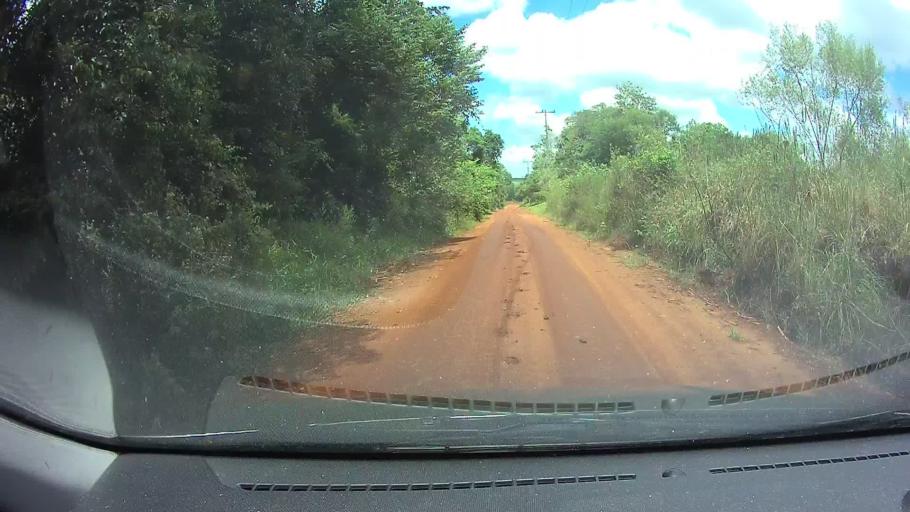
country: PY
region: Paraguari
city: La Colmena
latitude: -25.9480
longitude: -56.7816
